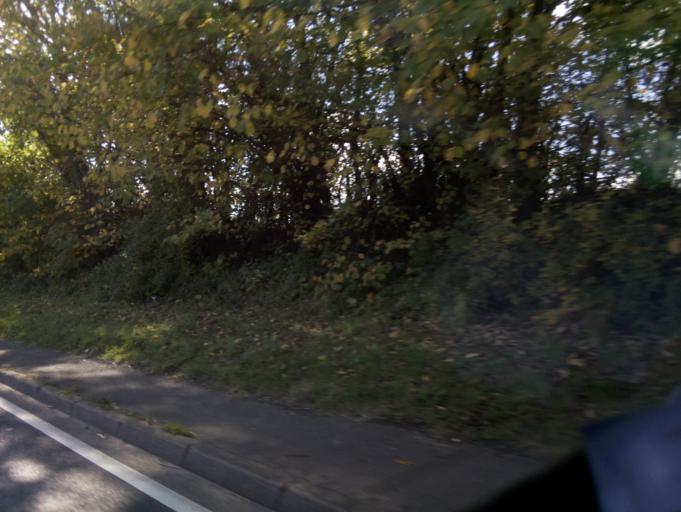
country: GB
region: Wales
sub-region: Sir Powys
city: Hay
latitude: 52.0335
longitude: -3.2050
